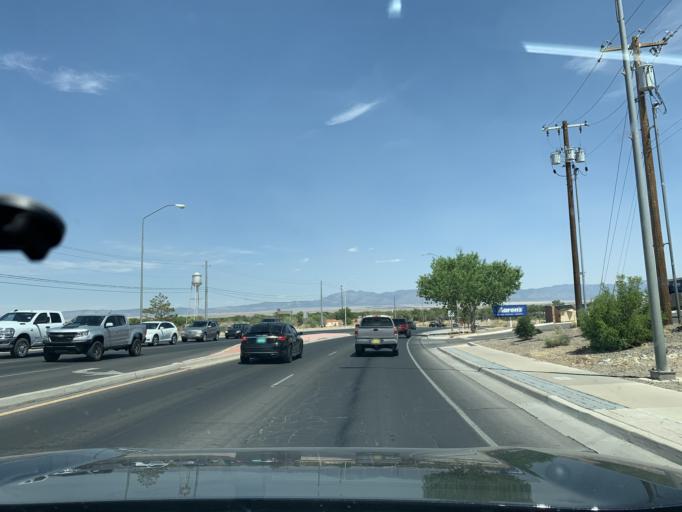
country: US
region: New Mexico
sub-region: Valencia County
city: Los Lunas
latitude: 34.8147
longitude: -106.7493
